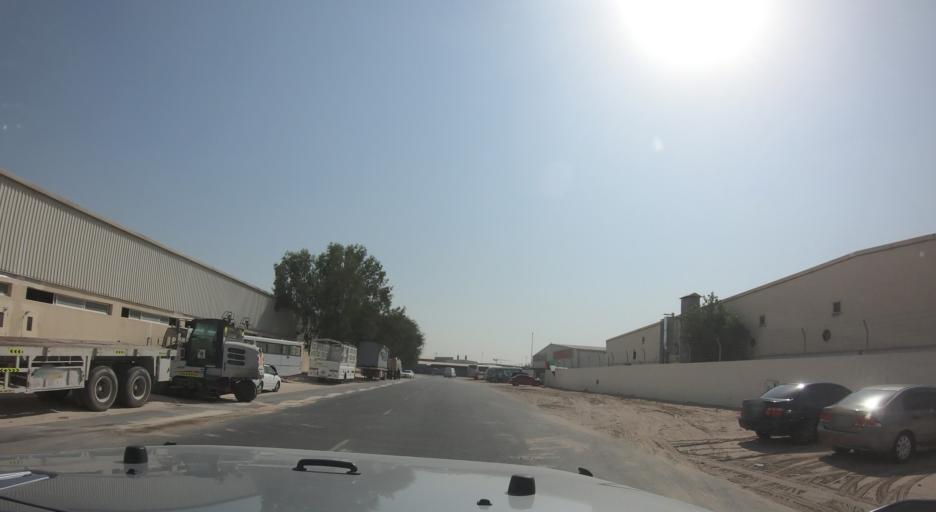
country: AE
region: Dubai
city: Dubai
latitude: 25.1512
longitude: 55.2334
